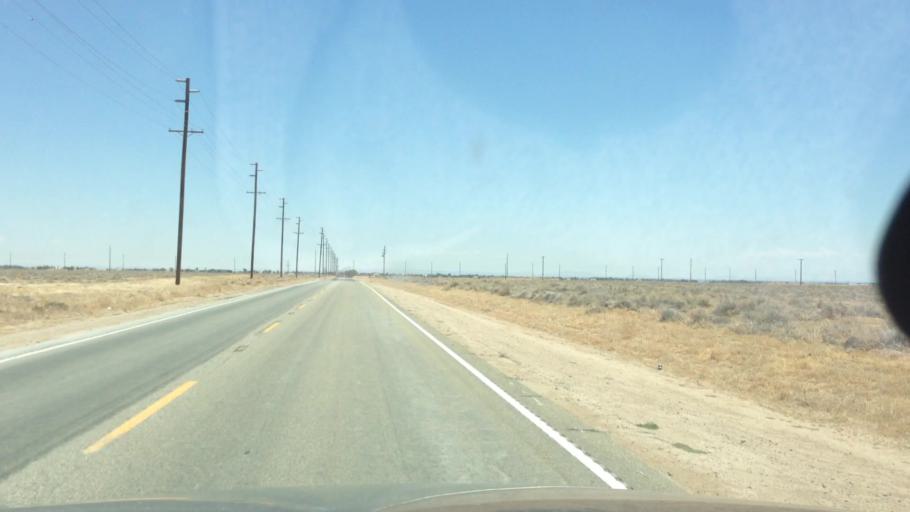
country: US
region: California
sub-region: Los Angeles County
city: Leona Valley
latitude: 34.7760
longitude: -118.3385
